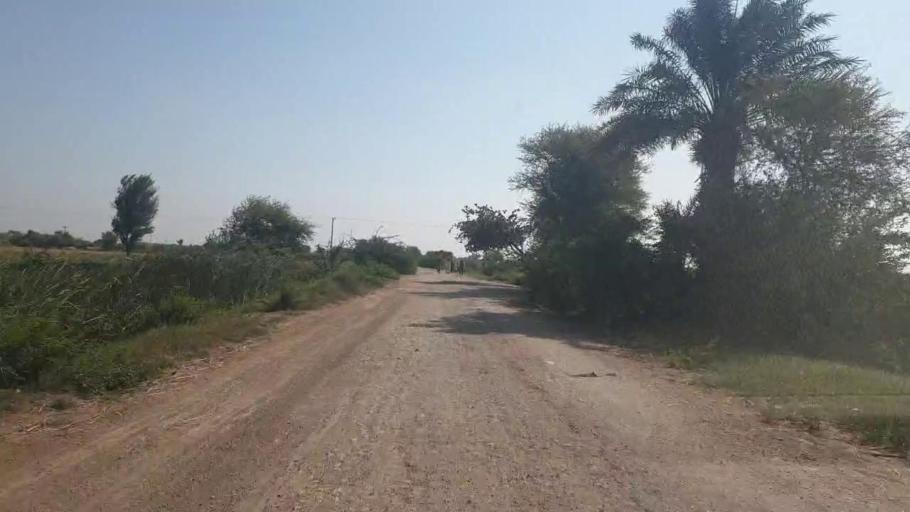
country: PK
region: Sindh
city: Badin
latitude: 24.5745
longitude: 68.8435
